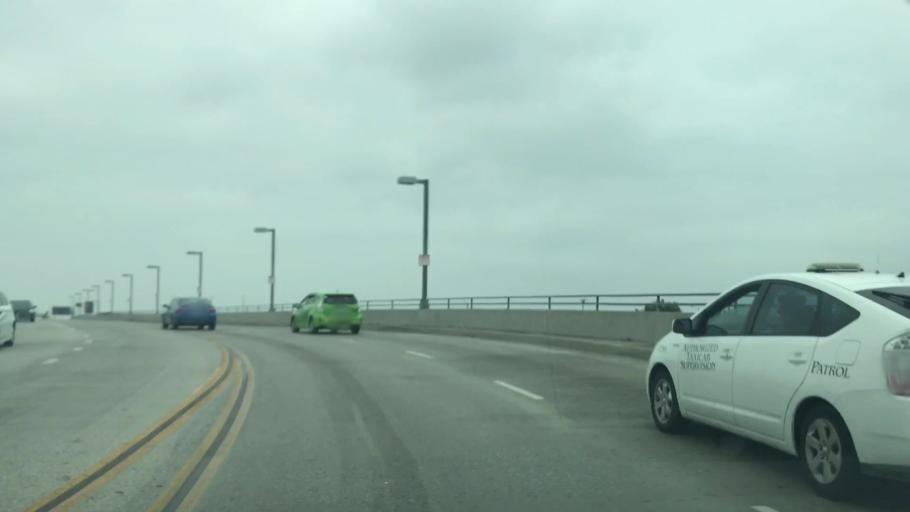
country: US
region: California
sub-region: Los Angeles County
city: El Segundo
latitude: 33.9497
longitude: -118.3946
